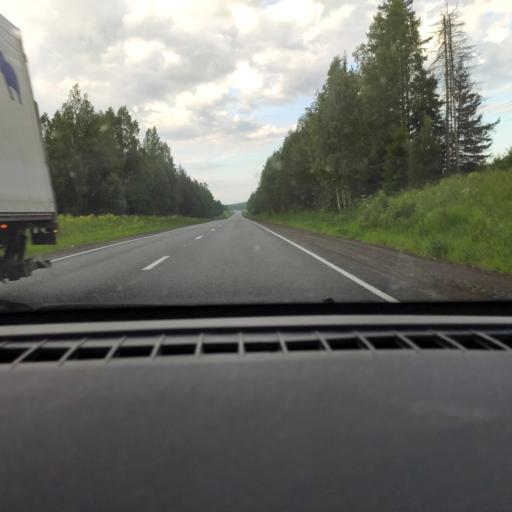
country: RU
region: Udmurtiya
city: Votkinsk
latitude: 57.2044
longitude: 54.1617
